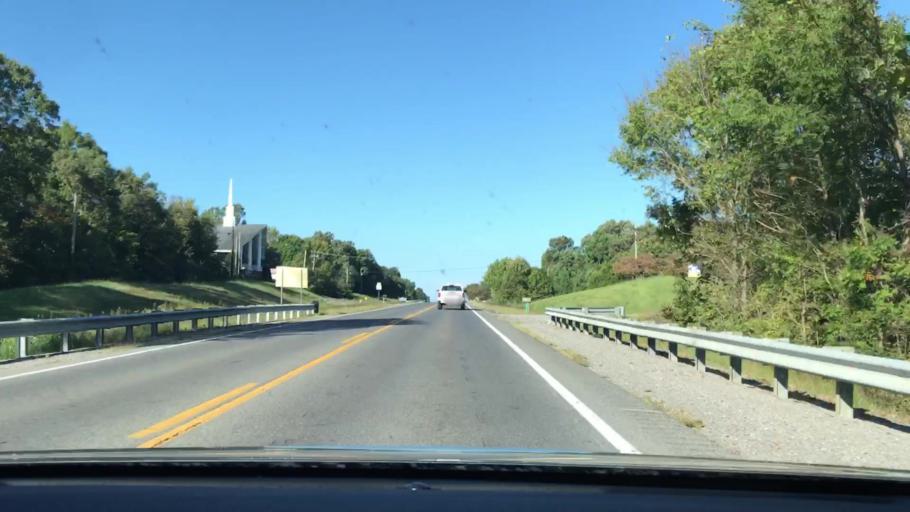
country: US
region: Kentucky
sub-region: Marshall County
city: Calvert City
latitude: 37.0045
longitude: -88.3698
